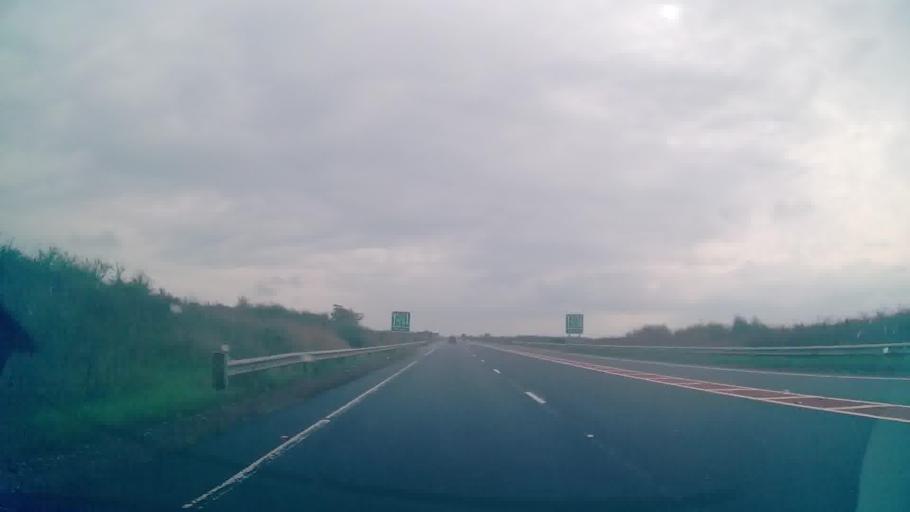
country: GB
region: Scotland
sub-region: Dumfries and Galloway
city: Lockerbie
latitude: 55.0219
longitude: -3.3731
